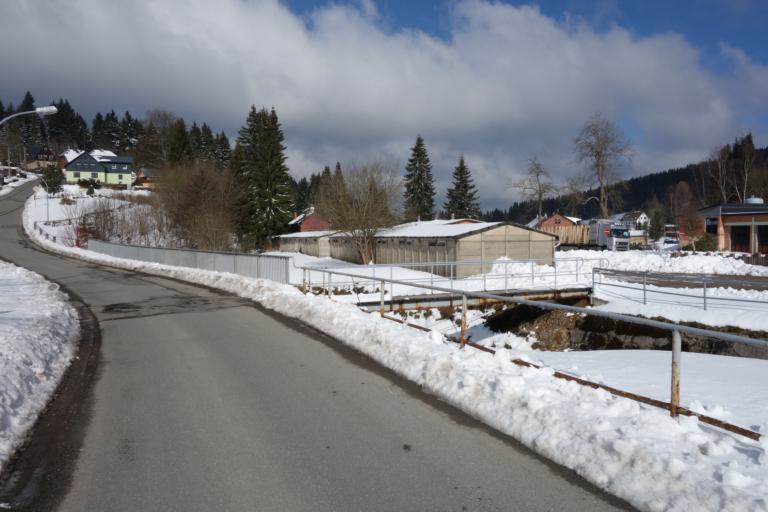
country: DE
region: Saxony
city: Eibenstock
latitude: 50.4348
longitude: 12.5852
